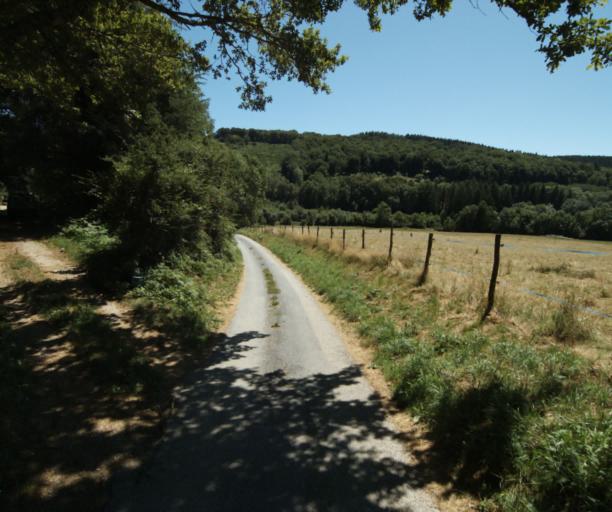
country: FR
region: Midi-Pyrenees
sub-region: Departement du Tarn
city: Dourgne
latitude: 43.4295
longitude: 2.1738
